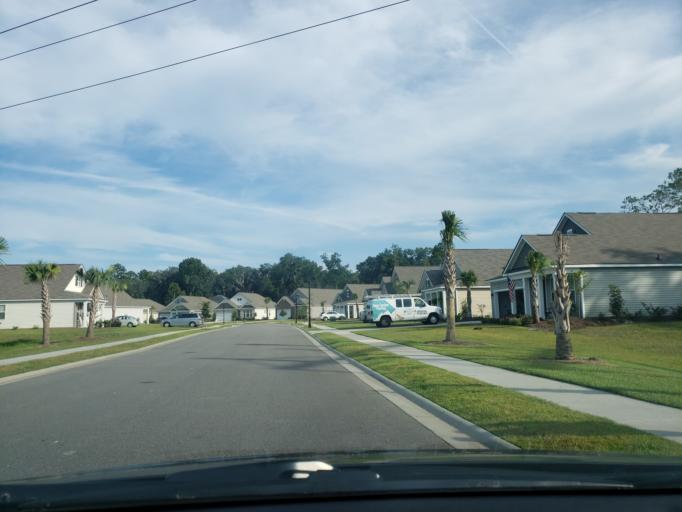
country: US
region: Georgia
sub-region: Chatham County
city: Montgomery
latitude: 31.9543
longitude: -81.1559
